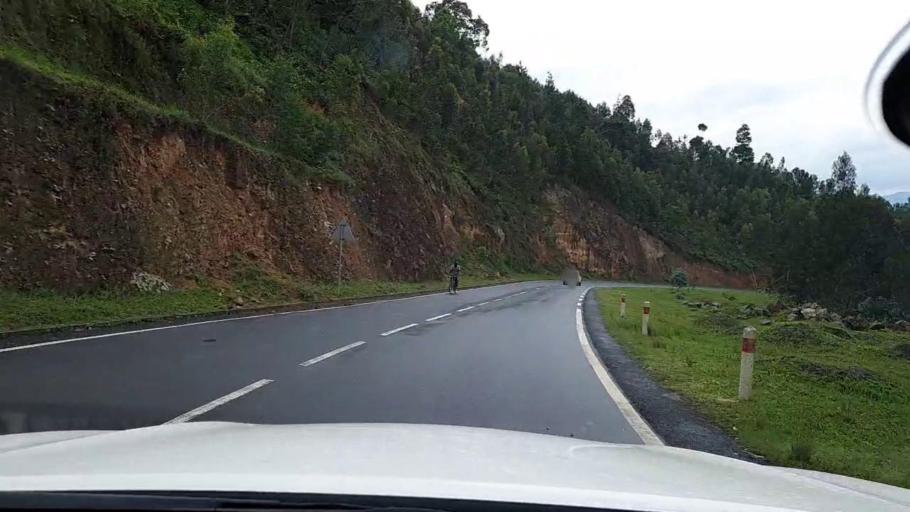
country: RW
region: Western Province
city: Kibuye
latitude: -2.1598
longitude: 29.2957
